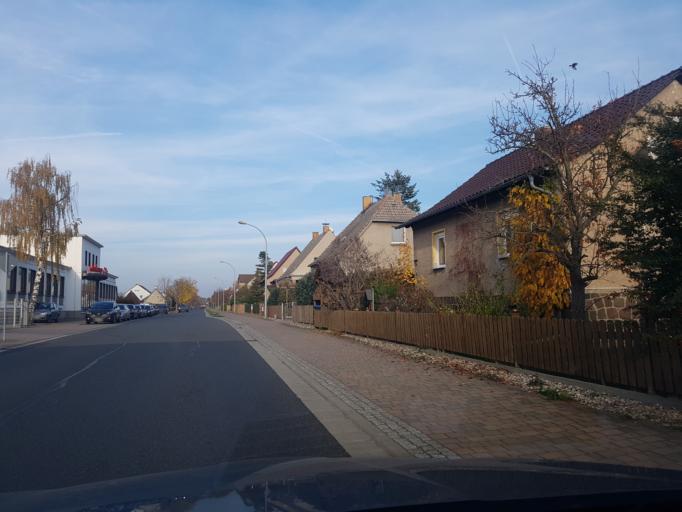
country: DE
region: Brandenburg
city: Falkenberg
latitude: 51.5769
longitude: 13.2308
